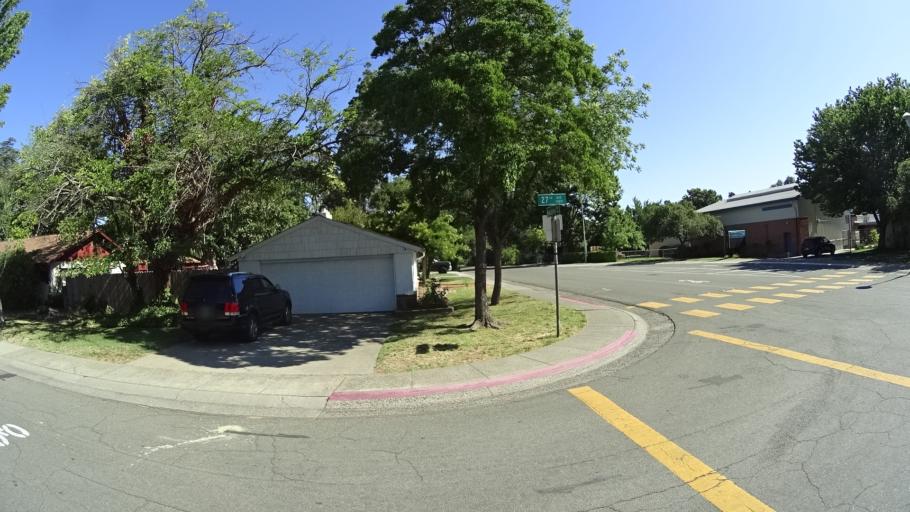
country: US
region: California
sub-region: Sacramento County
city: Sacramento
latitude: 38.5286
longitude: -121.5018
